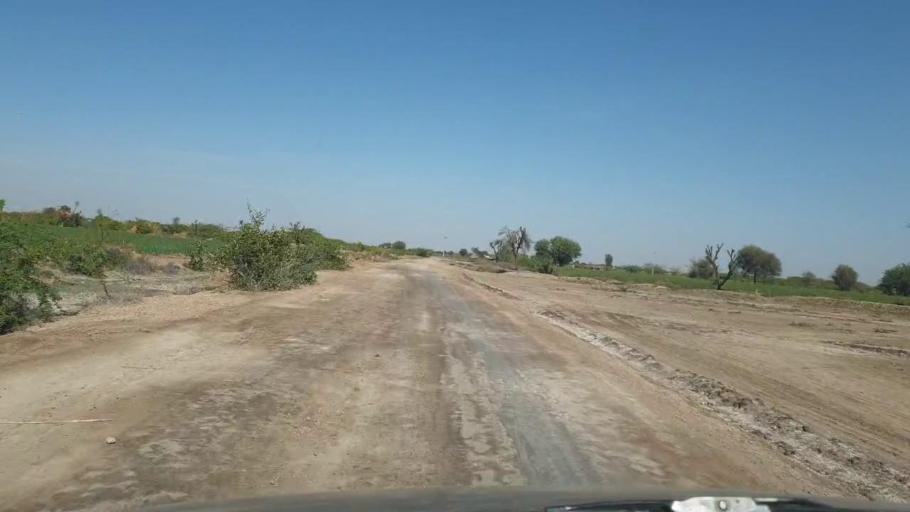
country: PK
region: Sindh
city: Dhoro Naro
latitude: 25.4120
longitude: 69.6171
